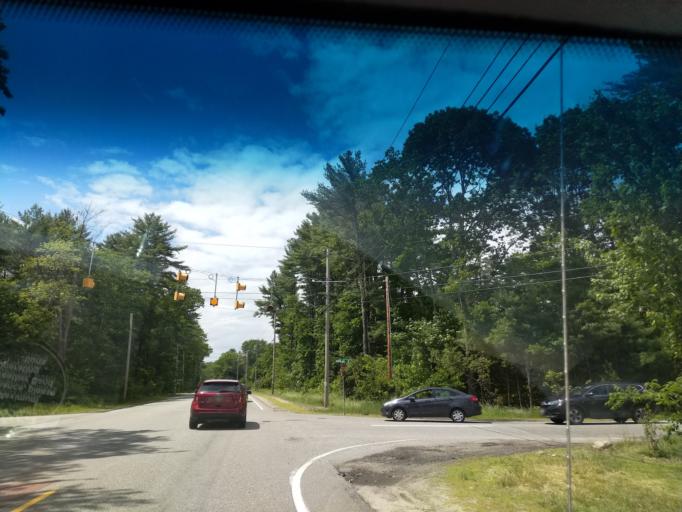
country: US
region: Maine
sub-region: Cumberland County
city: Westbrook
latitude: 43.6348
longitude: -70.3877
